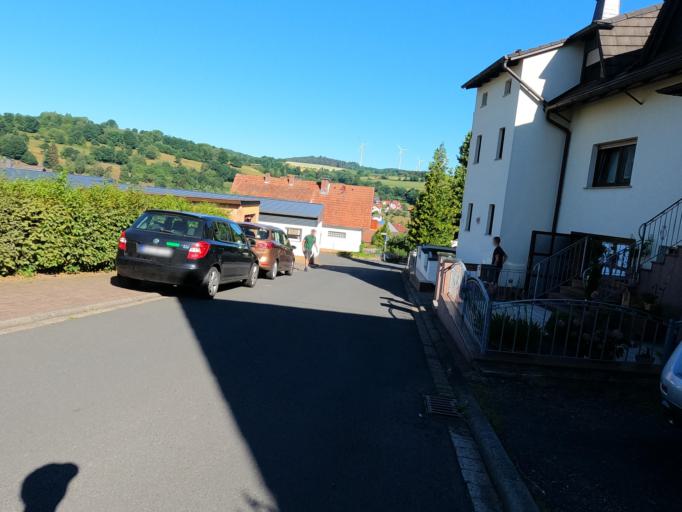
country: DE
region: Bavaria
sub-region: Regierungsbezirk Unterfranken
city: Zeitlofs
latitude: 50.3108
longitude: 9.6706
